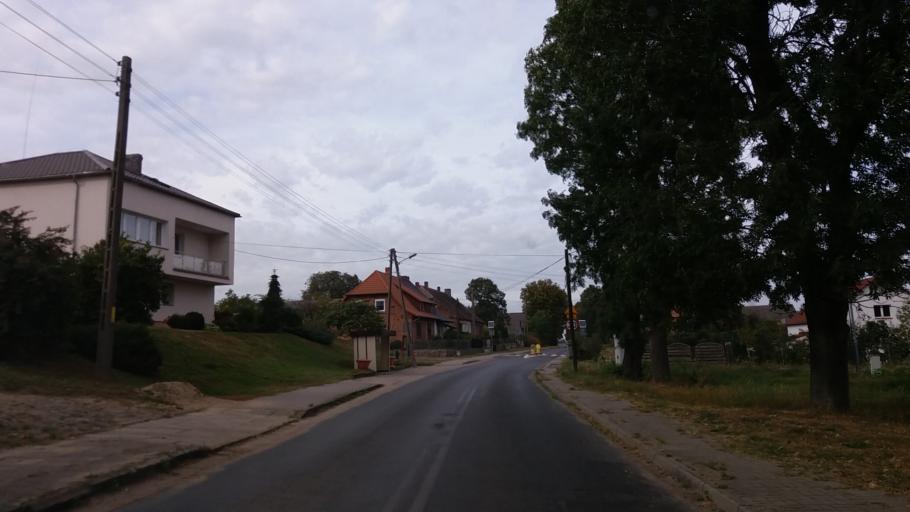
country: PL
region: Lubusz
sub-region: Powiat strzelecko-drezdenecki
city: Strzelce Krajenskie
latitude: 52.9239
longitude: 15.4812
